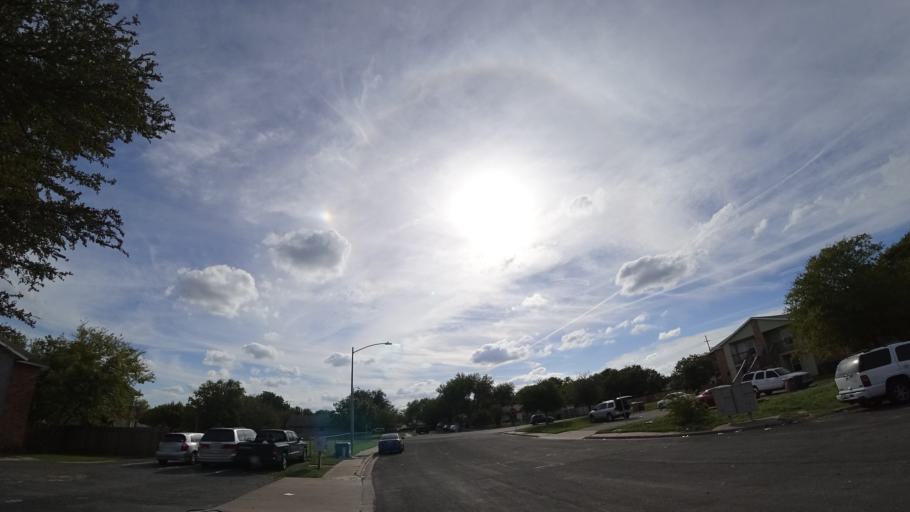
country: US
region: Texas
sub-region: Travis County
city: Austin
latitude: 30.2032
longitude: -97.7527
